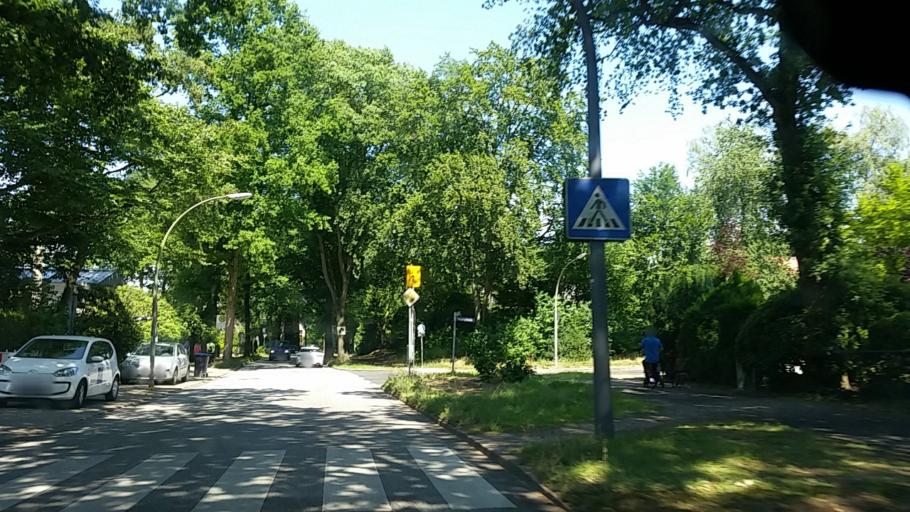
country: DE
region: Schleswig-Holstein
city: Wedel
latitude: 53.5726
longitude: 9.7578
